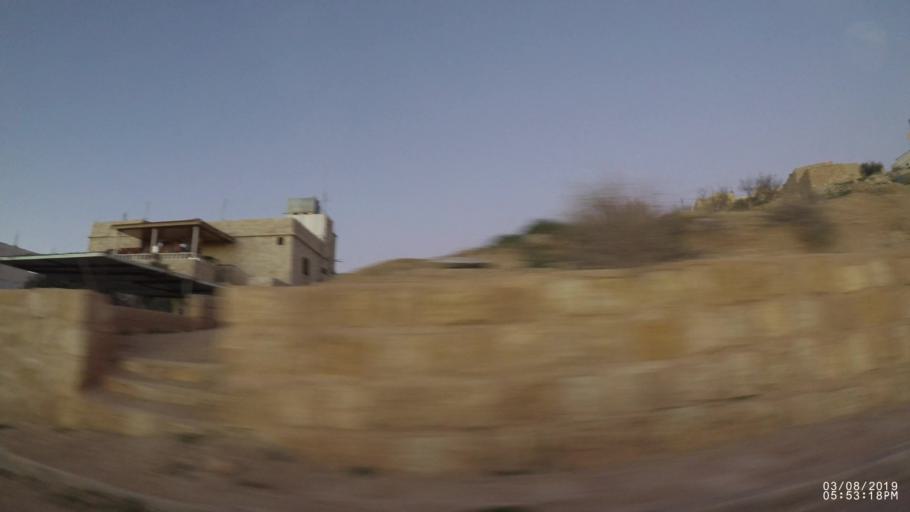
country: JO
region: Ma'an
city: Petra
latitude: 30.3239
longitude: 35.4809
